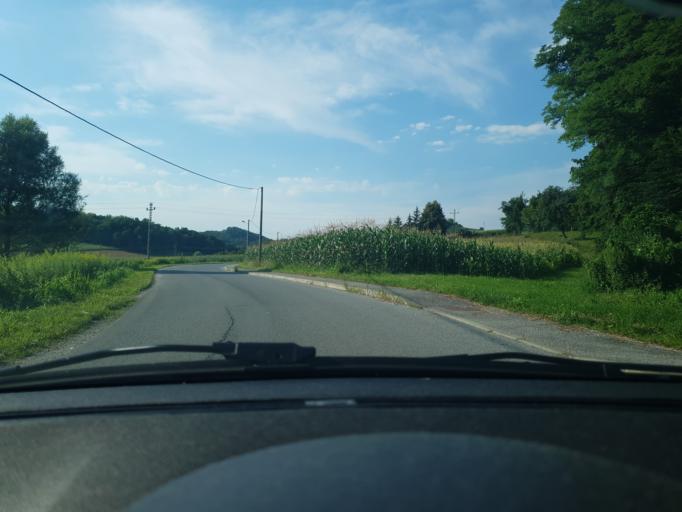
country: HR
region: Krapinsko-Zagorska
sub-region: Grad Krapina
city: Krapina
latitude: 46.1156
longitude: 15.8756
